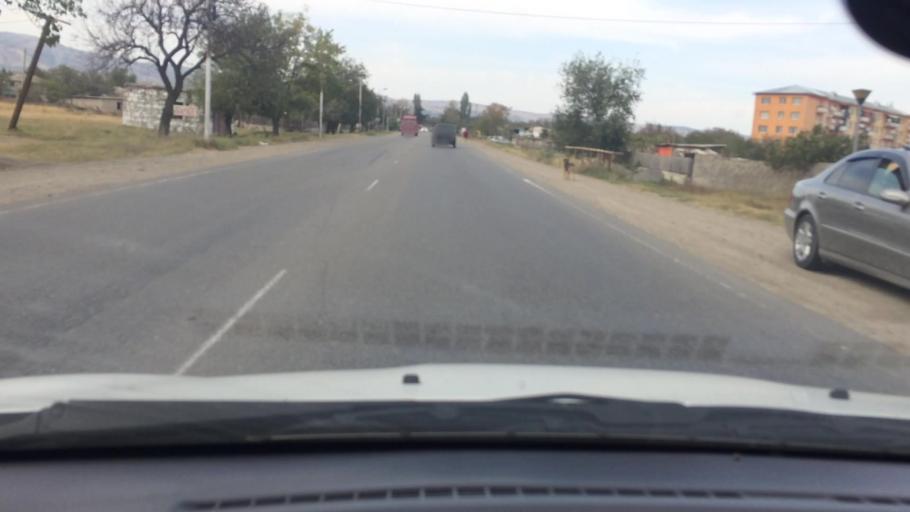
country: GE
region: Kvemo Kartli
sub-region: Marneuli
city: Marneuli
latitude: 41.5747
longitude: 44.7748
